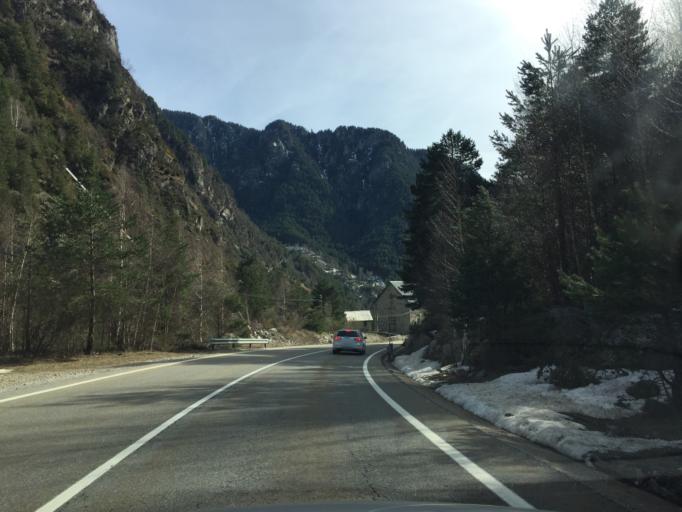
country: ES
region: Aragon
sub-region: Provincia de Huesca
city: Bielsa
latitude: 42.6773
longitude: 0.2142
